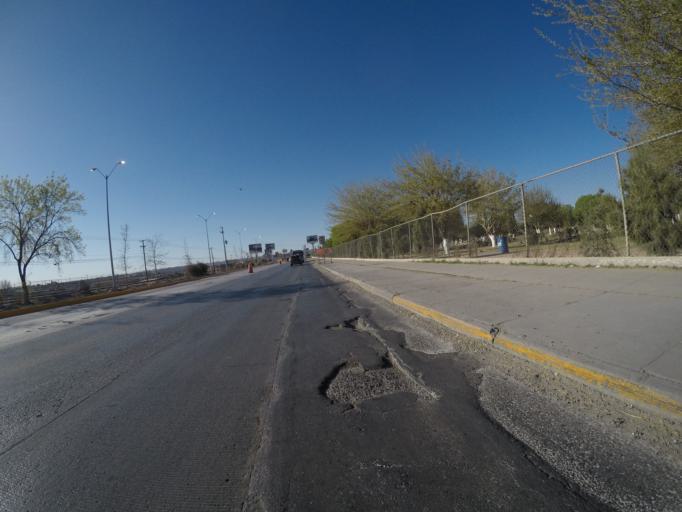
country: MX
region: Chihuahua
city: Ciudad Juarez
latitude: 31.6868
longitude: -106.4247
